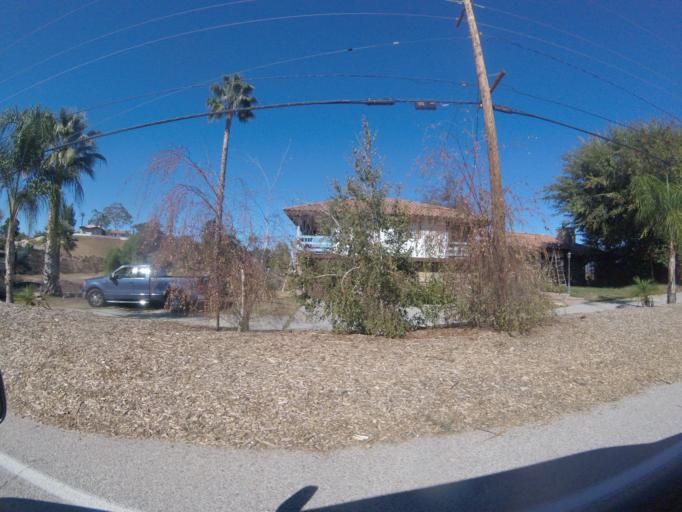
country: US
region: California
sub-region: San Bernardino County
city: Mentone
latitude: 34.0211
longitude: -117.1235
